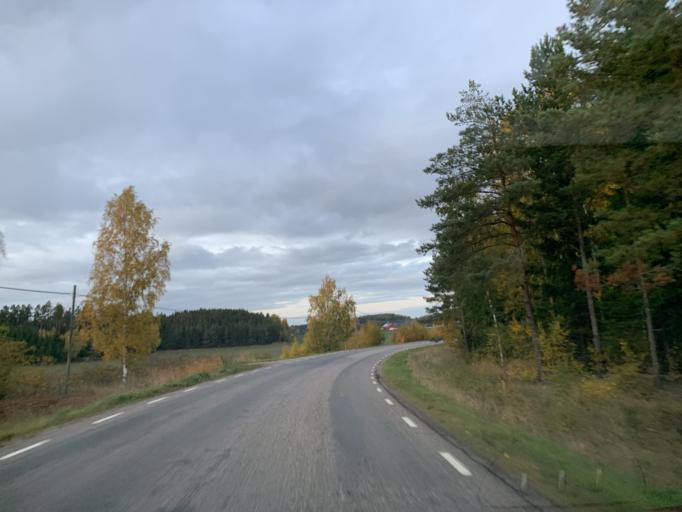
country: SE
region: Stockholm
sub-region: Nynashamns Kommun
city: Osmo
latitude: 58.9473
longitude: 17.7621
